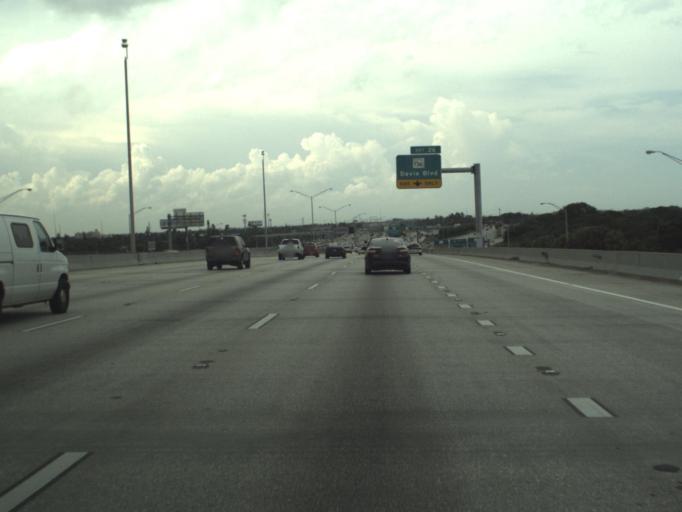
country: US
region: Florida
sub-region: Broward County
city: Boulevard Gardens
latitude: 26.0982
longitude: -80.1687
